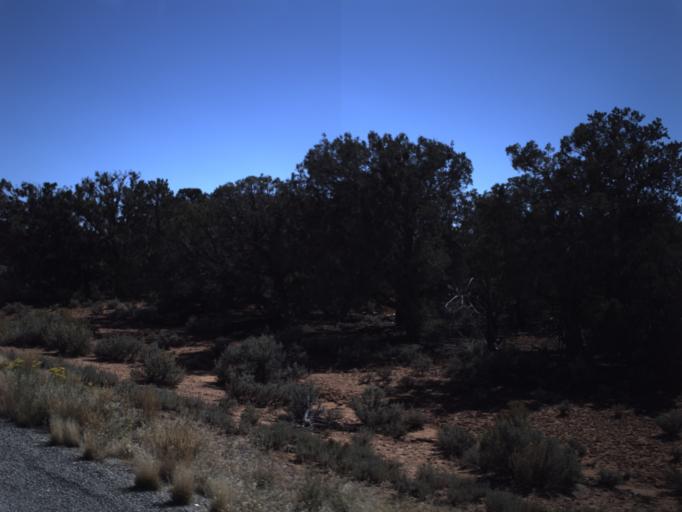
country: US
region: Utah
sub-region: San Juan County
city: Blanding
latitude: 37.5405
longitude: -109.9663
